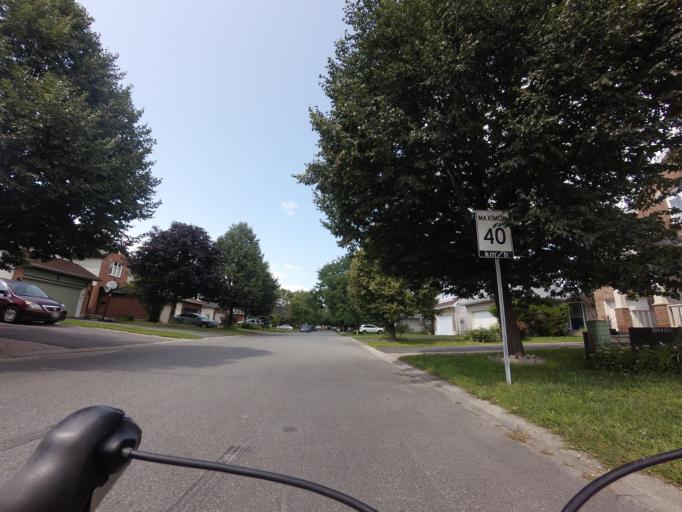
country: CA
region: Ontario
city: Bells Corners
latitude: 45.2809
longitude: -75.8552
